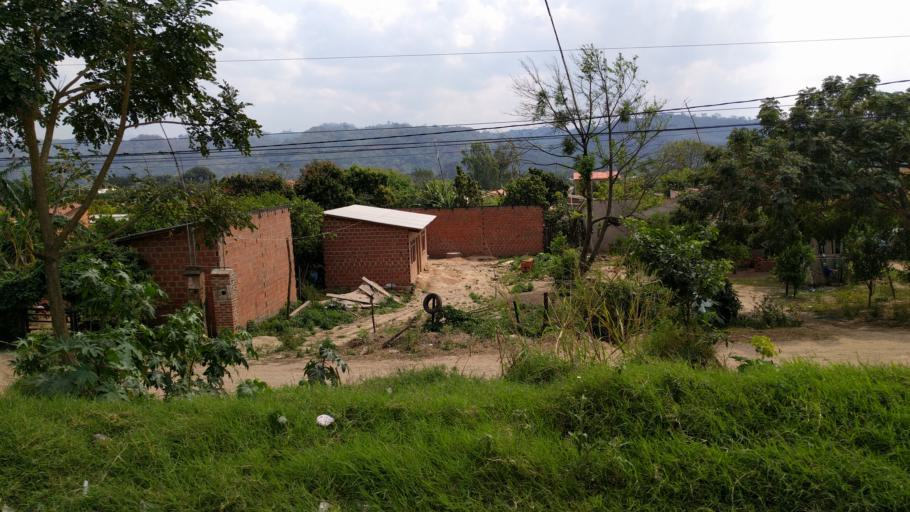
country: BO
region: Santa Cruz
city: Limoncito
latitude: -18.0223
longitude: -63.3992
